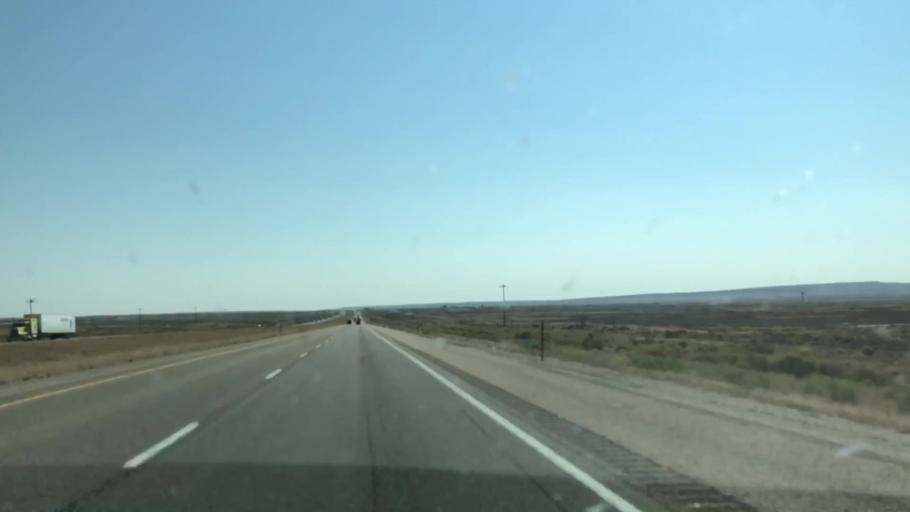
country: US
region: Wyoming
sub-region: Sweetwater County
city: Rock Springs
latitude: 41.6374
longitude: -108.4496
